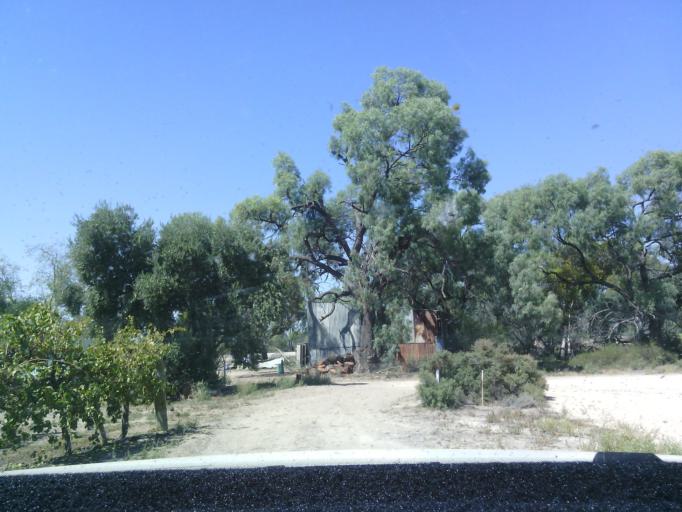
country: AU
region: South Australia
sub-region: Renmark Paringa
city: Renmark
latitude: -34.2120
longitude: 140.7457
